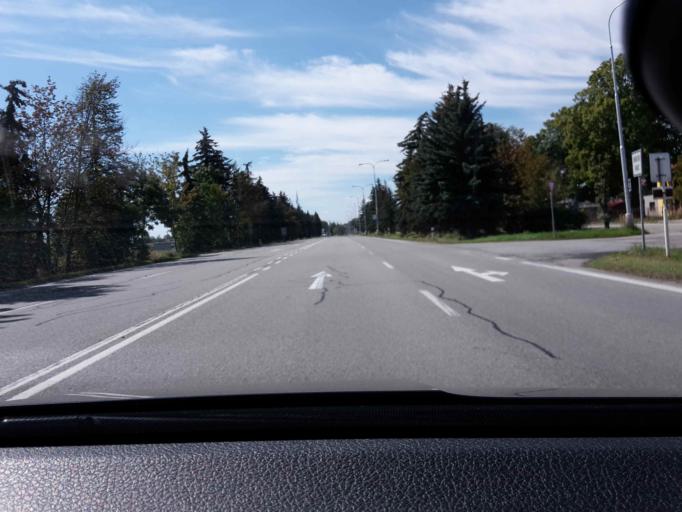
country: CZ
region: Jihocesky
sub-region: Okres Jindrichuv Hradec
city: Jindrichuv Hradec
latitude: 49.1590
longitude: 15.0235
